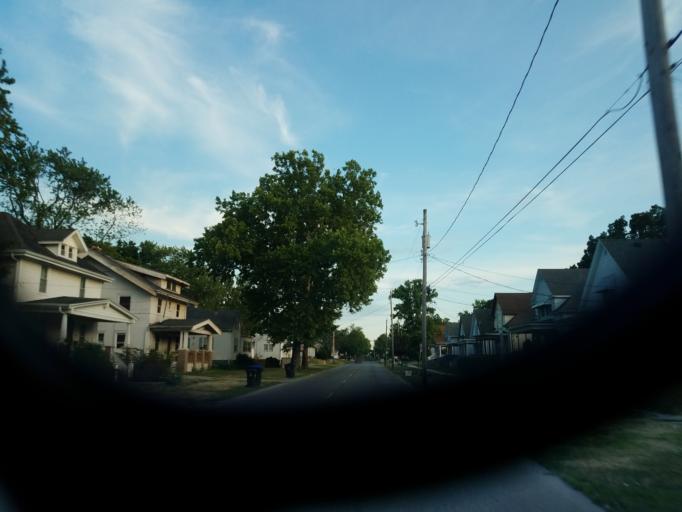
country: US
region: Illinois
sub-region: McLean County
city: Bloomington
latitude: 40.4685
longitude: -88.9941
